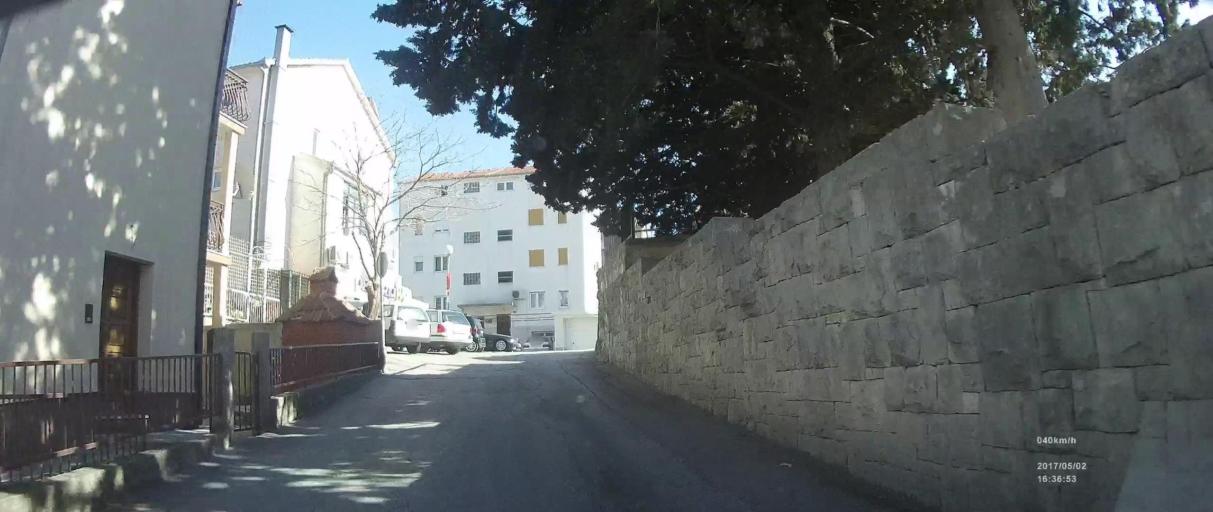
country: HR
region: Splitsko-Dalmatinska
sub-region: Grad Split
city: Stobrec
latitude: 43.5035
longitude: 16.5212
